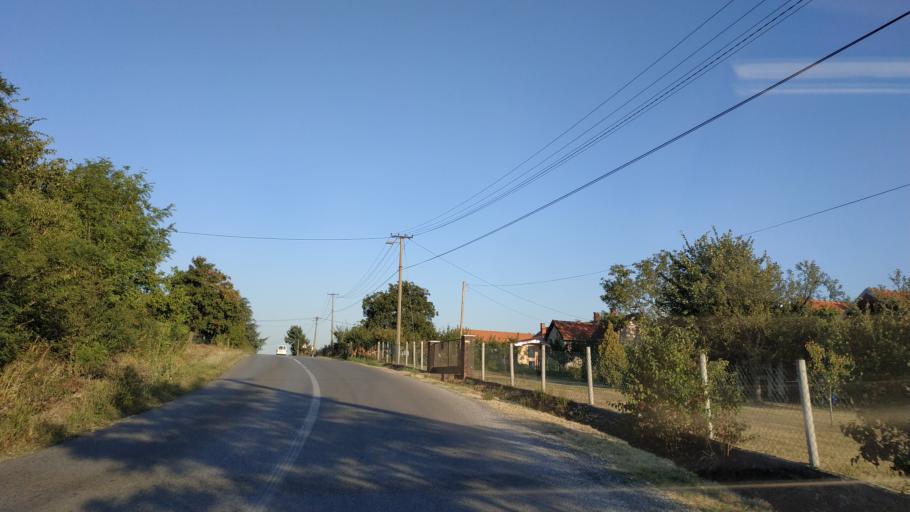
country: RS
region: Central Serbia
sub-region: Sumadijski Okrug
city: Topola
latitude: 44.2733
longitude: 20.6338
